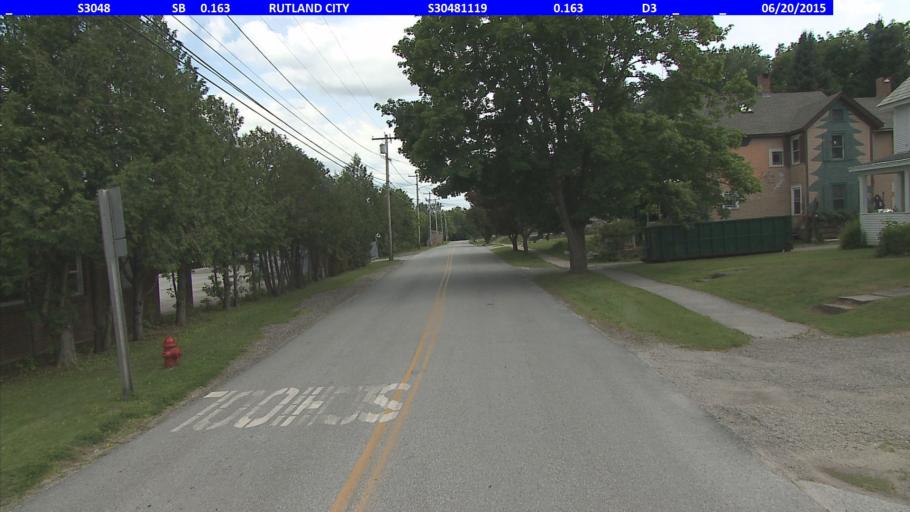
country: US
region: Vermont
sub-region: Rutland County
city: Rutland
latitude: 43.6111
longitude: -72.9917
